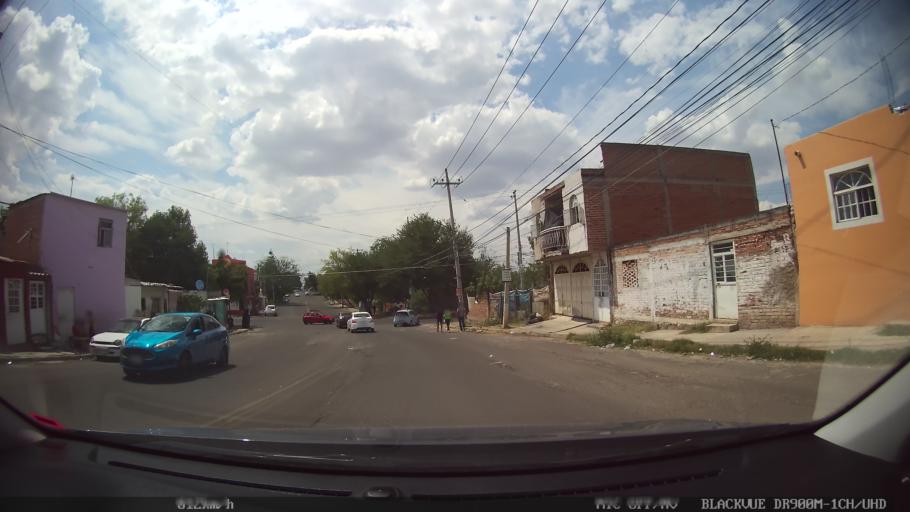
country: MX
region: Jalisco
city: Tonala
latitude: 20.6212
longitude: -103.2529
